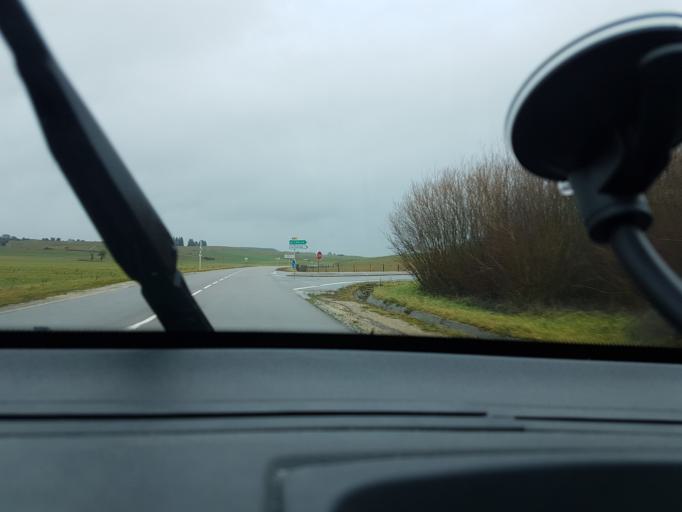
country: FR
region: Franche-Comte
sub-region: Departement du Doubs
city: Vercel-Villedieu-le-Camp
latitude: 47.1462
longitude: 6.4454
